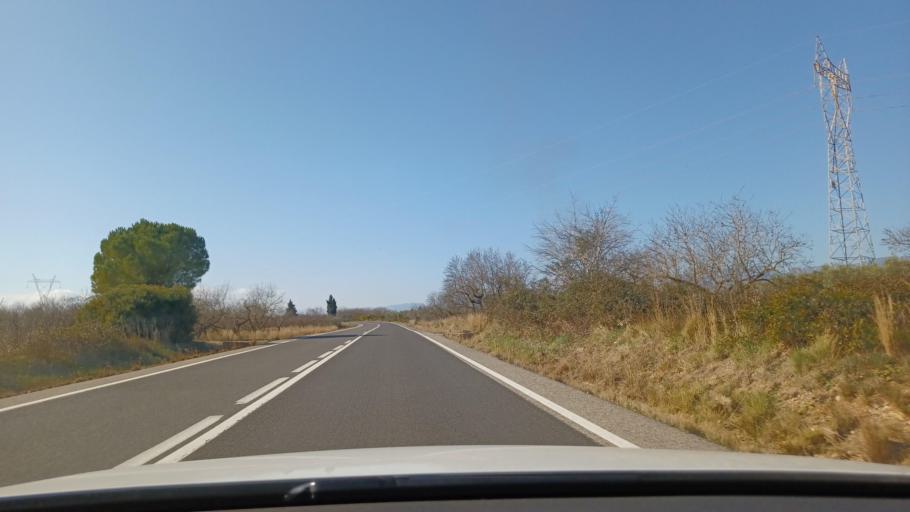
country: ES
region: Catalonia
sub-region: Provincia de Tarragona
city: Santa Barbara
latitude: 40.6776
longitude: 0.4539
